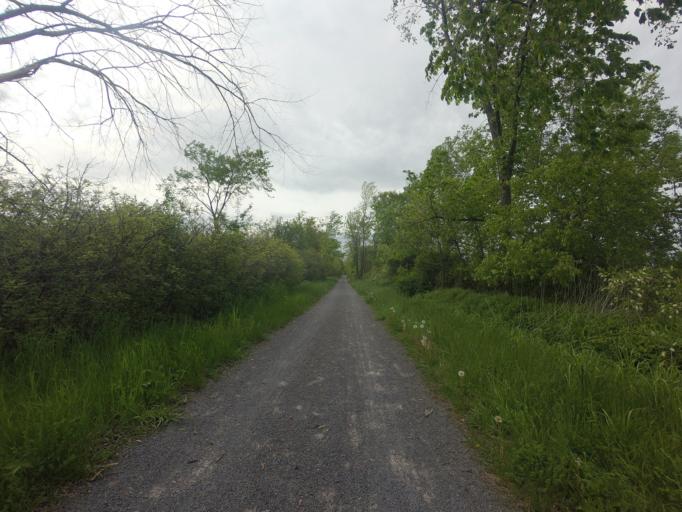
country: CA
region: Ontario
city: Kingston
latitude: 44.3527
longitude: -76.6177
